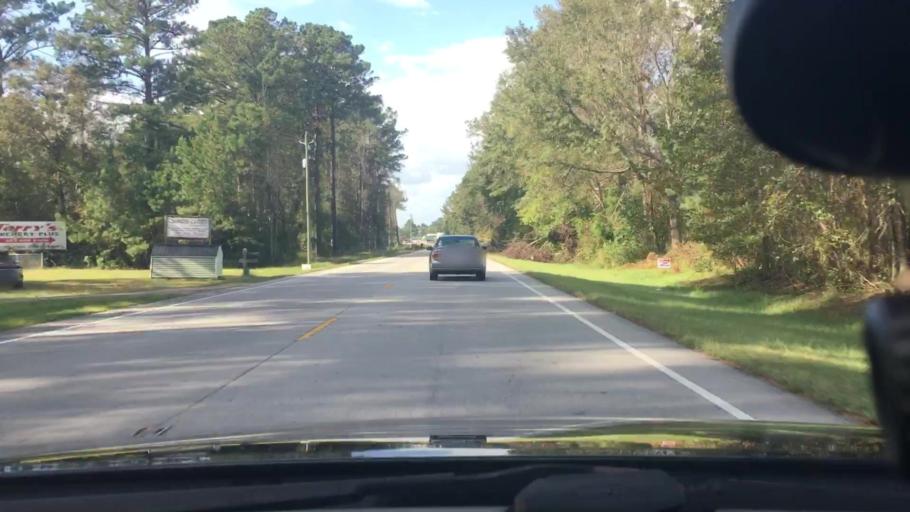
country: US
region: North Carolina
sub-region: Craven County
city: New Bern
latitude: 35.2152
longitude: -77.0634
